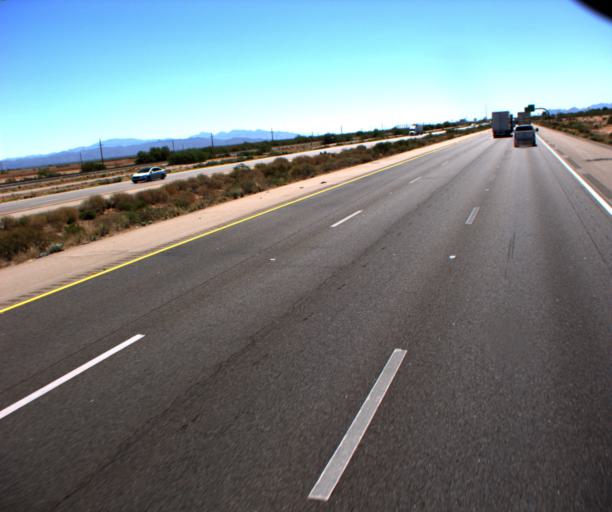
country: US
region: Arizona
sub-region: Pima County
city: Avra Valley
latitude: 32.5898
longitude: -111.3371
